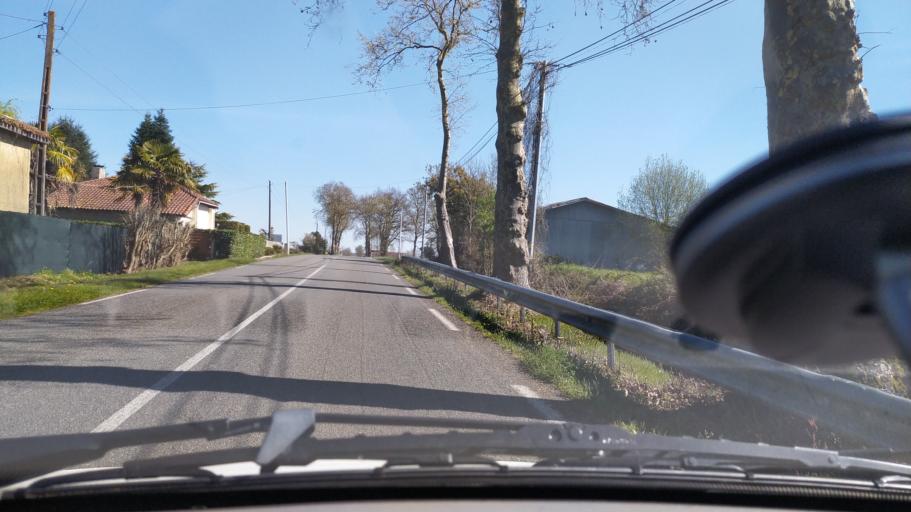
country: FR
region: Midi-Pyrenees
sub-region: Departement du Gers
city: Le Houga
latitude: 43.7626
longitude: -0.1113
